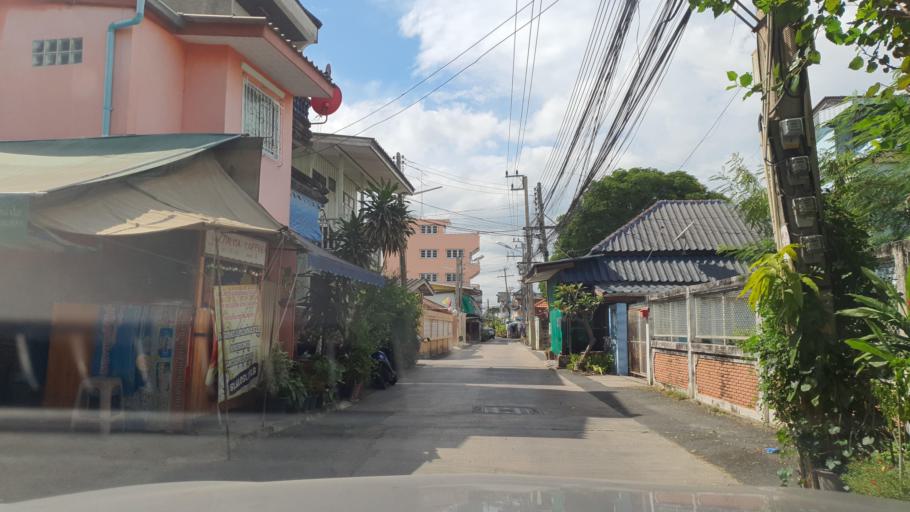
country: TH
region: Chon Buri
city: Chon Buri
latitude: 13.3697
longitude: 100.9843
